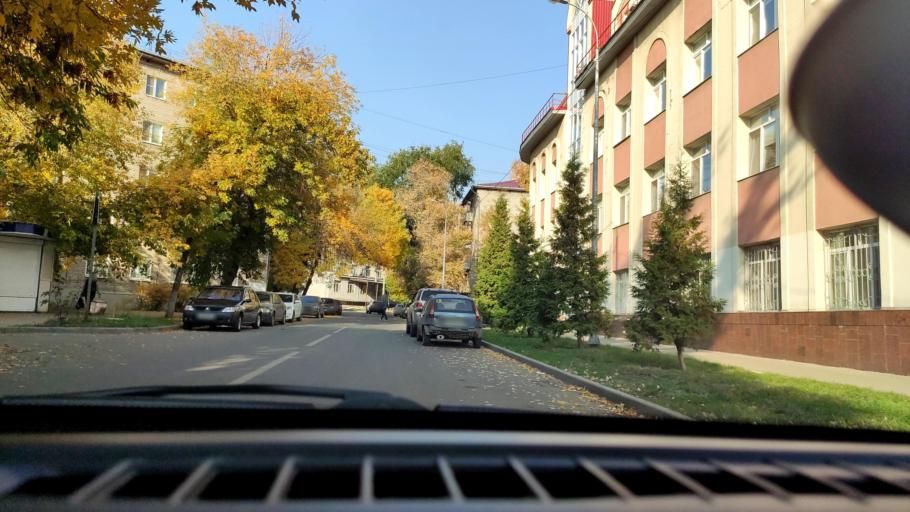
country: RU
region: Samara
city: Samara
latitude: 53.1925
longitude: 50.1310
